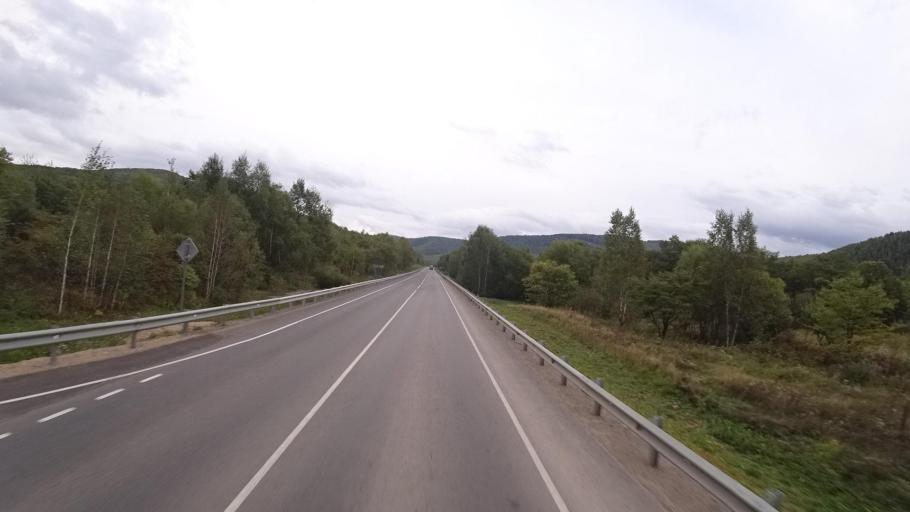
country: RU
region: Jewish Autonomous Oblast
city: Khingansk
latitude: 48.9865
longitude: 131.1370
